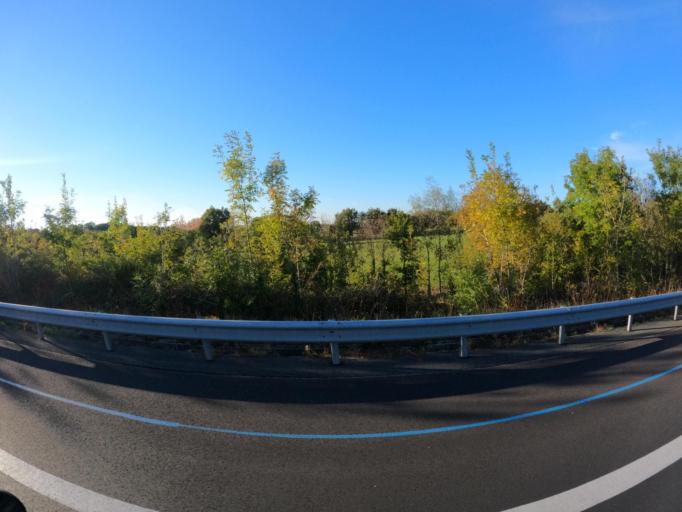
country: FR
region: Pays de la Loire
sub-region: Departement de la Vendee
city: La Verrie
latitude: 46.9306
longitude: -1.0131
